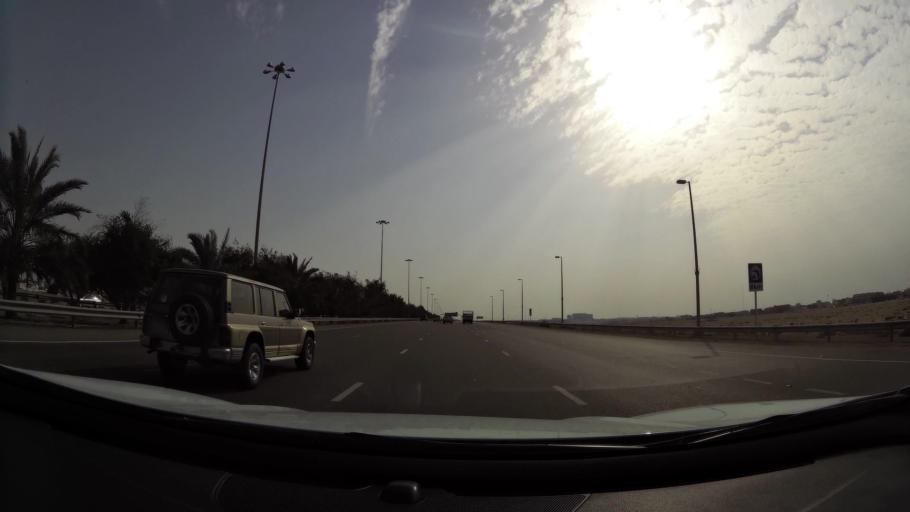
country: AE
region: Abu Dhabi
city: Abu Dhabi
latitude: 24.3515
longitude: 54.6439
